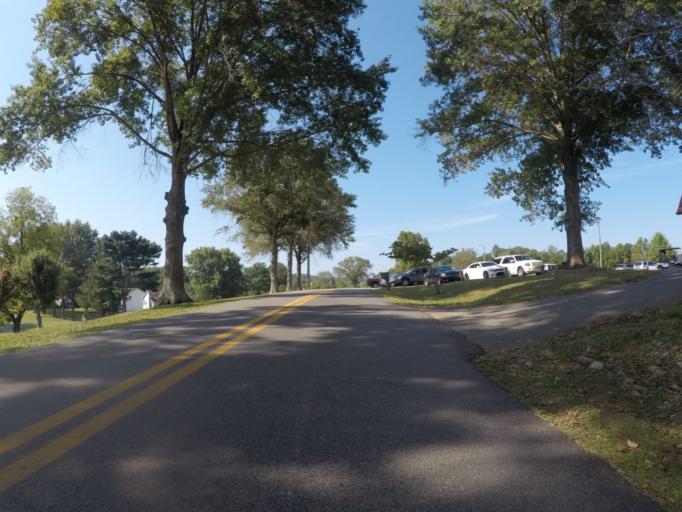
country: US
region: West Virginia
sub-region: Cabell County
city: Barboursville
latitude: 38.3674
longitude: -82.2661
